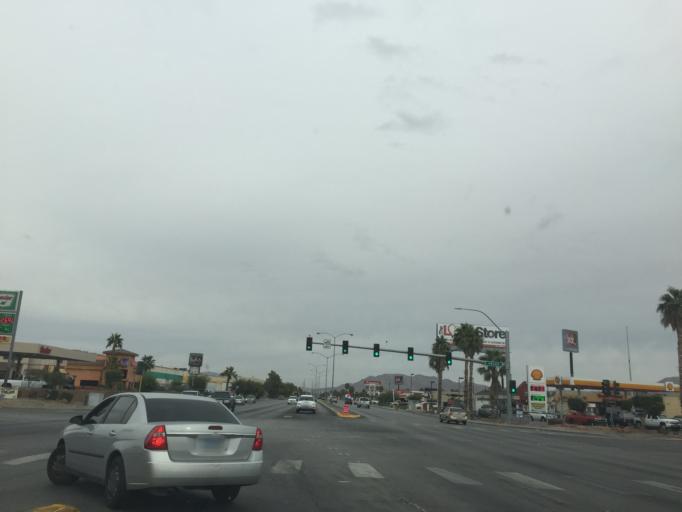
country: US
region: Nevada
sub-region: Clark County
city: Sunrise Manor
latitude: 36.2403
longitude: -115.0977
